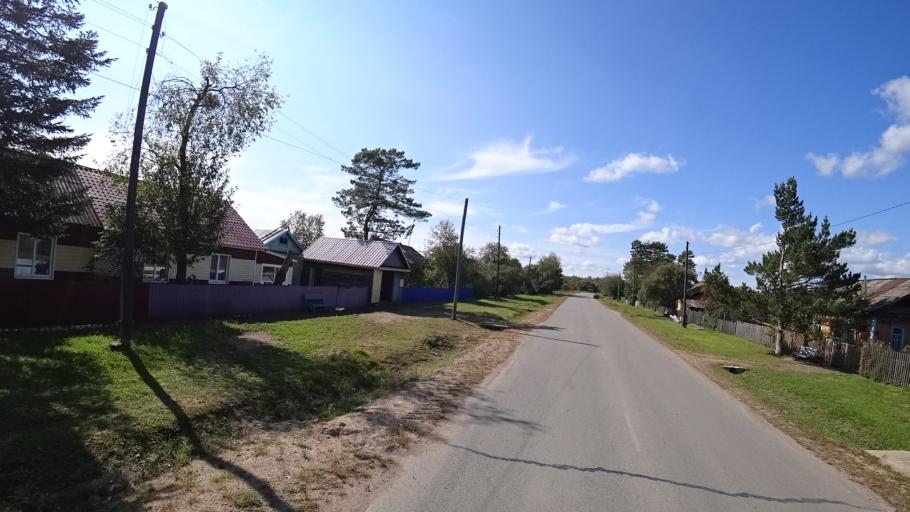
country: RU
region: Amur
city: Arkhara
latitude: 49.4036
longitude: 130.1341
